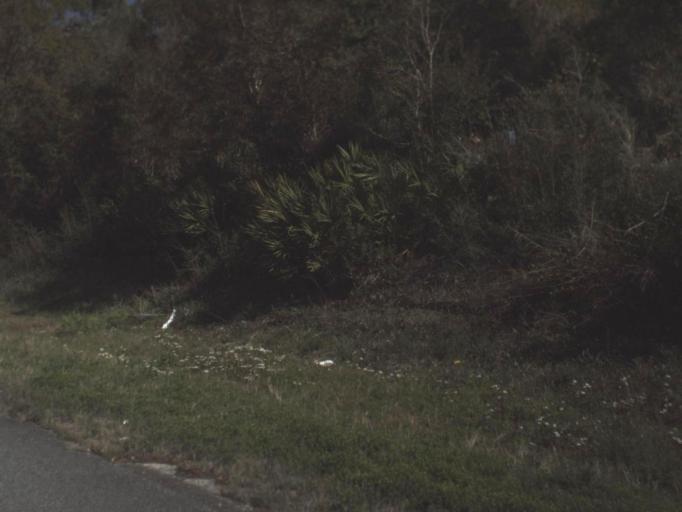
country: US
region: Florida
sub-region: Franklin County
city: Carrabelle
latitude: 29.8256
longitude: -84.7032
